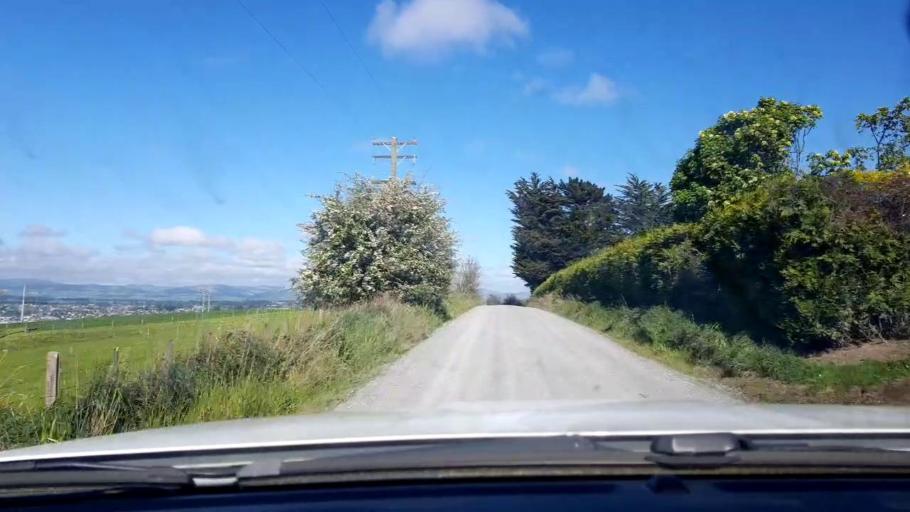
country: NZ
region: Otago
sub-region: Clutha District
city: Balclutha
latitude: -46.2235
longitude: 169.7594
